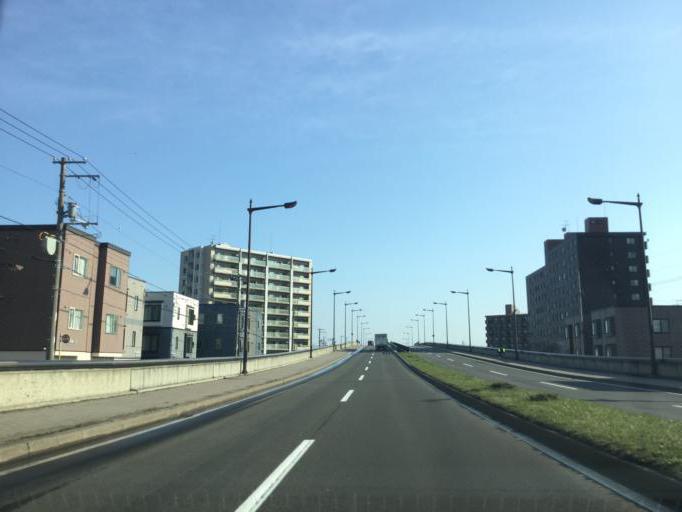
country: JP
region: Hokkaido
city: Ebetsu
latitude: 43.0452
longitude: 141.4687
